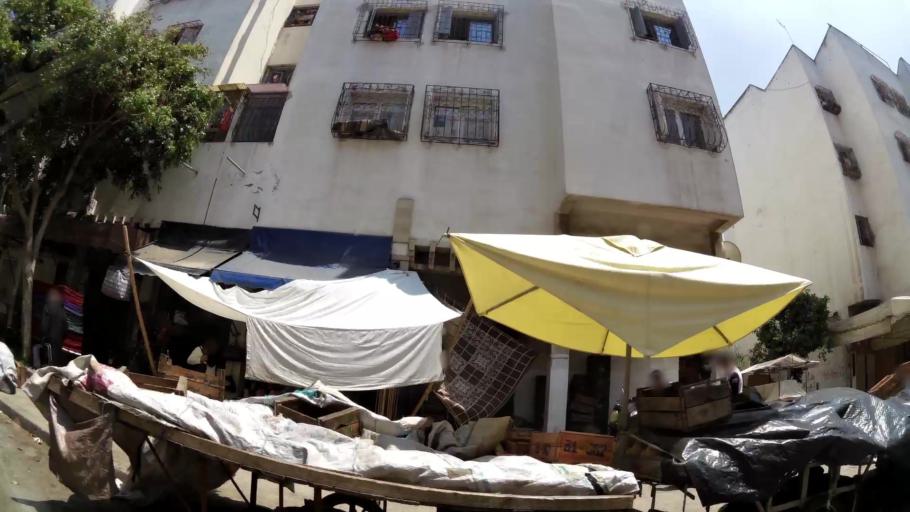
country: MA
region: Rabat-Sale-Zemmour-Zaer
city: Sale
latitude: 34.0622
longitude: -6.7932
